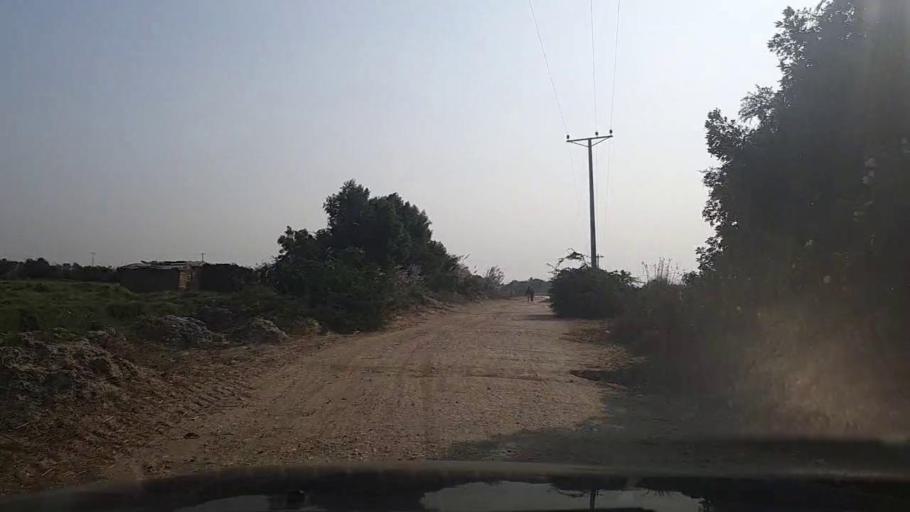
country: PK
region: Sindh
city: Mirpur Sakro
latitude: 24.6305
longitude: 67.7564
